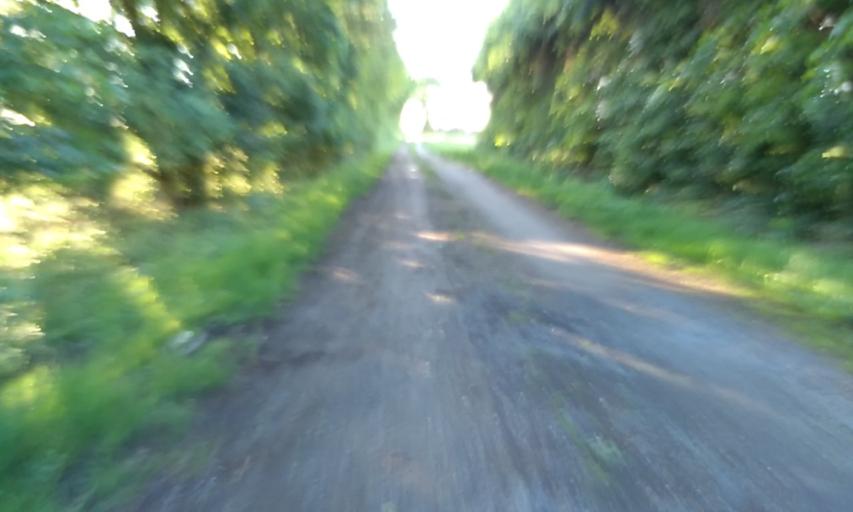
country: DE
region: Lower Saxony
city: Bliedersdorf
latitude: 53.4891
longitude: 9.5701
